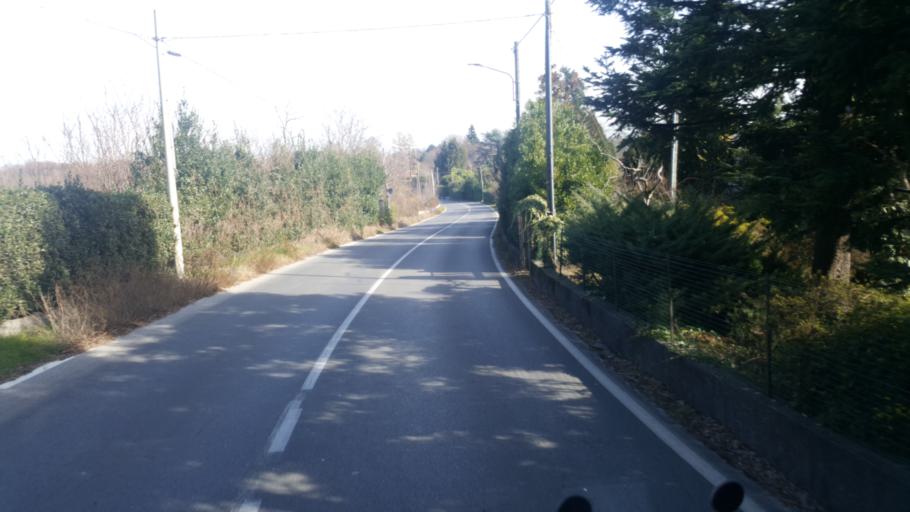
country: IT
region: Lombardy
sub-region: Provincia di Varese
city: Cadrezzate
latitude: 45.8056
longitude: 8.6550
